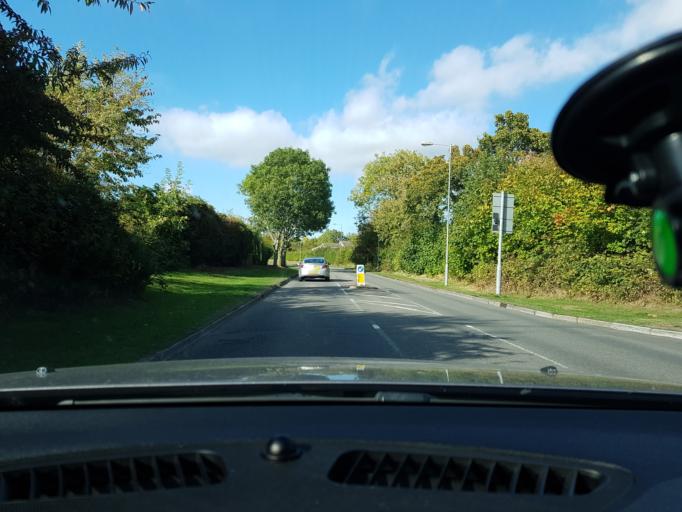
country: GB
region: England
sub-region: Borough of Swindon
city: Chiseldon
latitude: 51.5467
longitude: -1.7347
